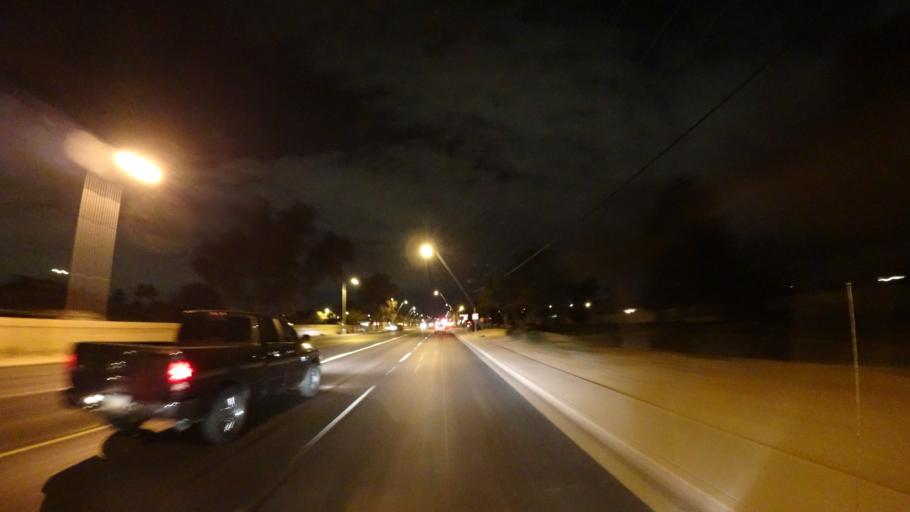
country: US
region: Arizona
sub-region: Maricopa County
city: San Carlos
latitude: 33.3457
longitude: -111.8590
